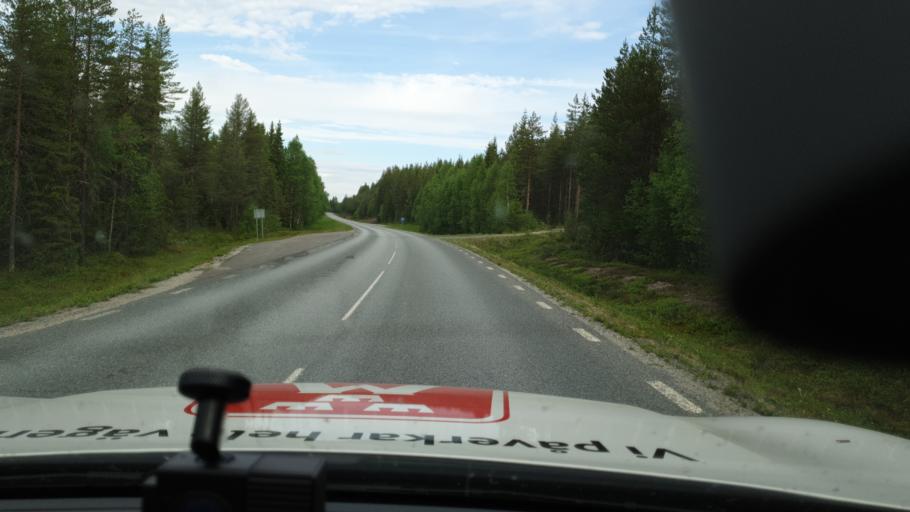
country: SE
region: Vaesterbotten
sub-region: Mala Kommun
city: Mala
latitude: 65.0139
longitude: 18.4508
